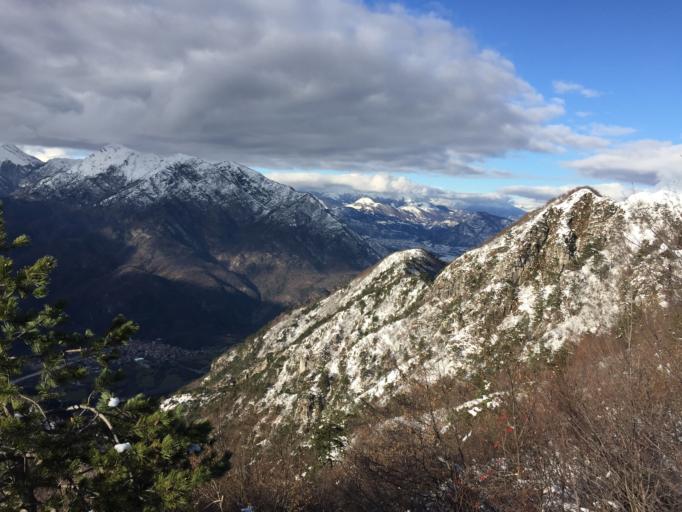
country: IT
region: Friuli Venezia Giulia
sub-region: Provincia di Udine
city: Trasaghis
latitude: 46.2984
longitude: 13.0839
